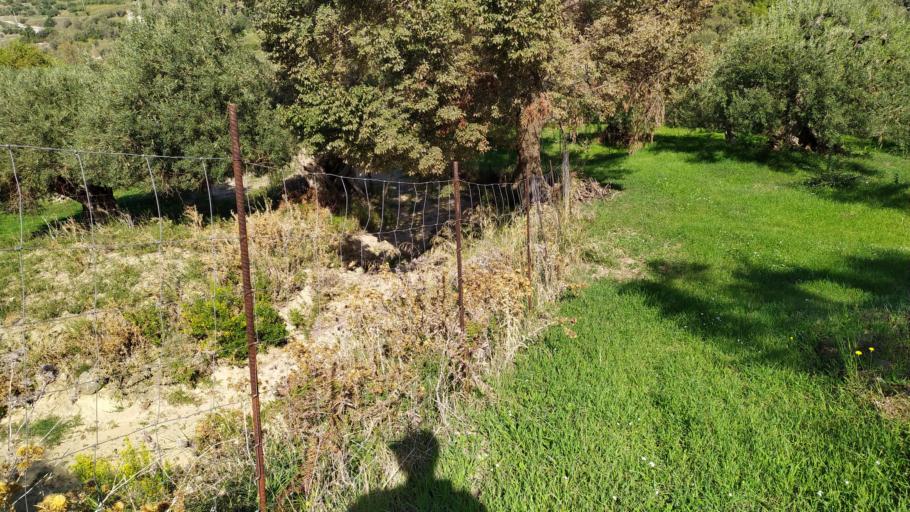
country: IT
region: Sicily
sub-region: Messina
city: Gualtieri Sicamino
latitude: 38.1604
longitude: 15.2982
